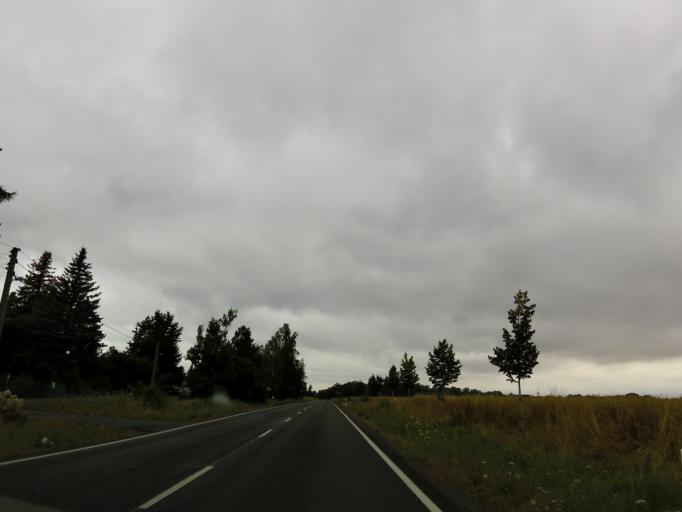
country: DE
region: Saxony
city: Markkleeberg
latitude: 51.2674
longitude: 12.4324
